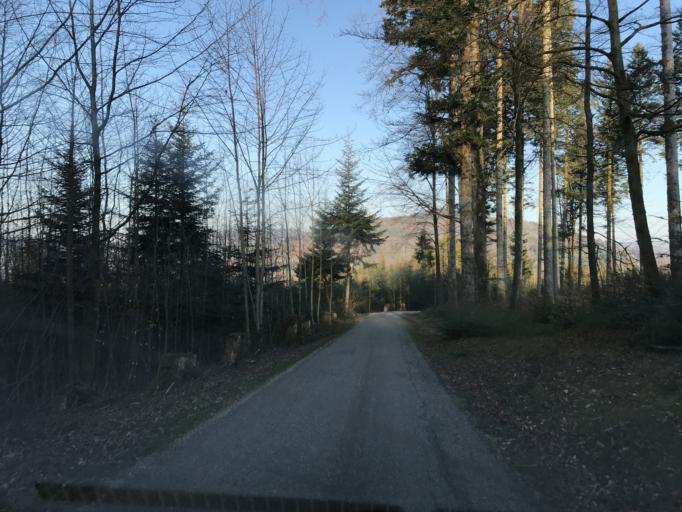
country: DE
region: Baden-Wuerttemberg
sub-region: Freiburg Region
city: Hausen
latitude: 47.6954
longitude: 7.8283
